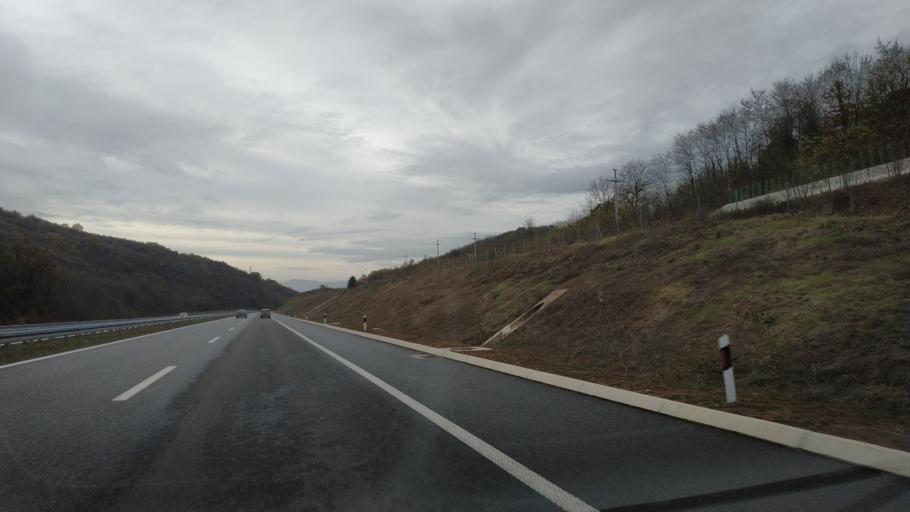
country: RS
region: Central Serbia
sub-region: Nisavski Okrug
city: Niska Banja
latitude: 43.2979
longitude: 22.0743
